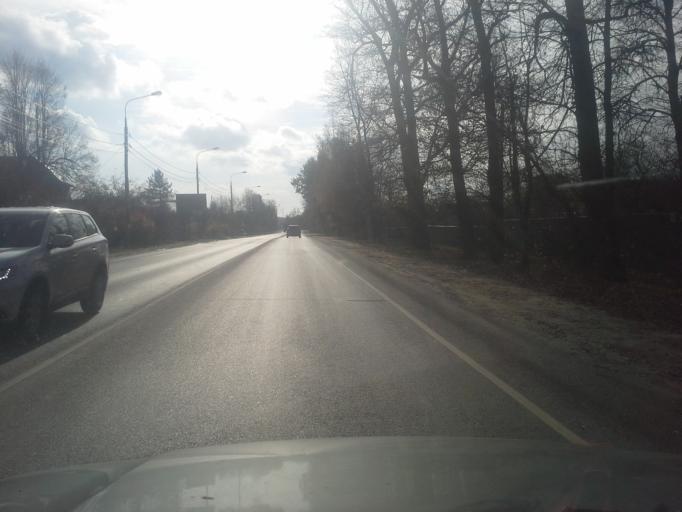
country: RU
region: Moskovskaya
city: Zvenigorod
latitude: 55.7263
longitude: 36.8617
